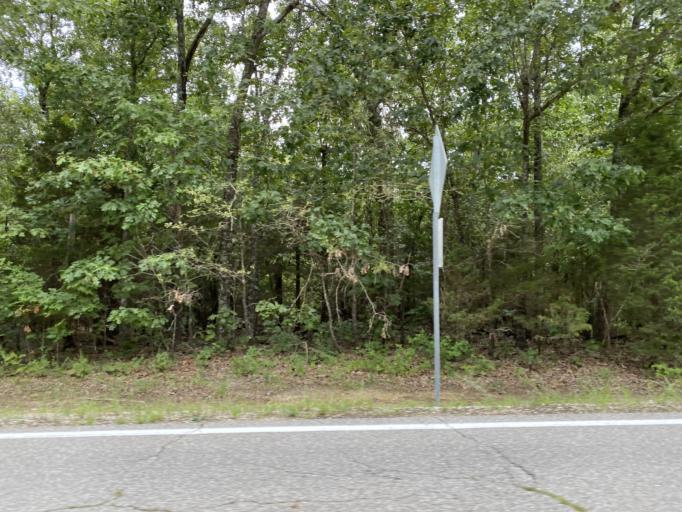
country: US
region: Arkansas
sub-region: Fulton County
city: Salem
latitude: 36.4205
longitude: -91.7155
